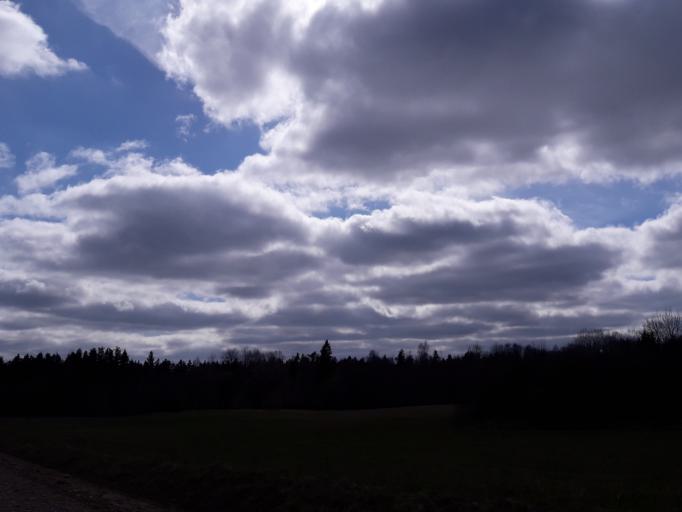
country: LV
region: Talsu Rajons
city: Sabile
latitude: 56.9110
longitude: 22.3987
